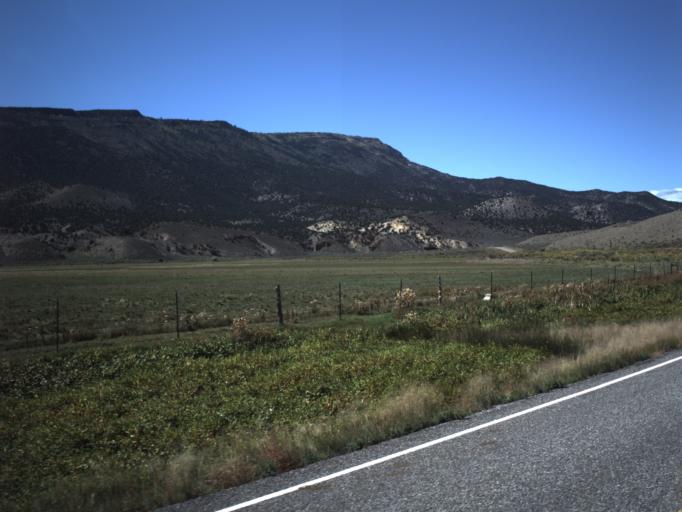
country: US
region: Utah
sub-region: Piute County
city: Junction
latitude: 38.1687
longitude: -112.0423
